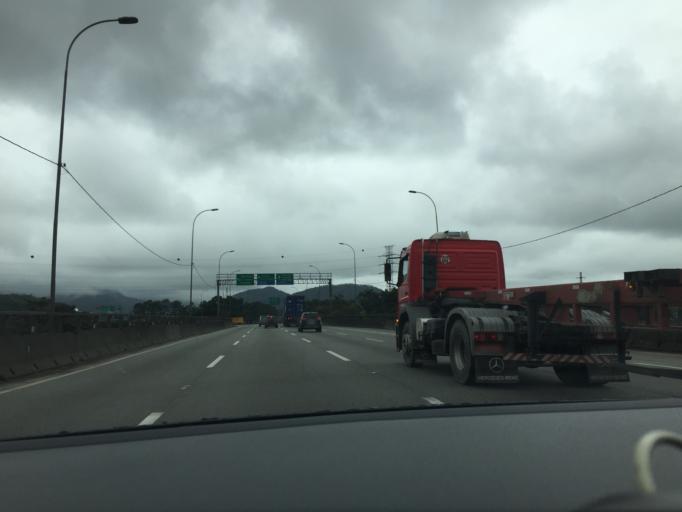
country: BR
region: Sao Paulo
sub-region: Cubatao
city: Cubatao
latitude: -23.8891
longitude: -46.4333
